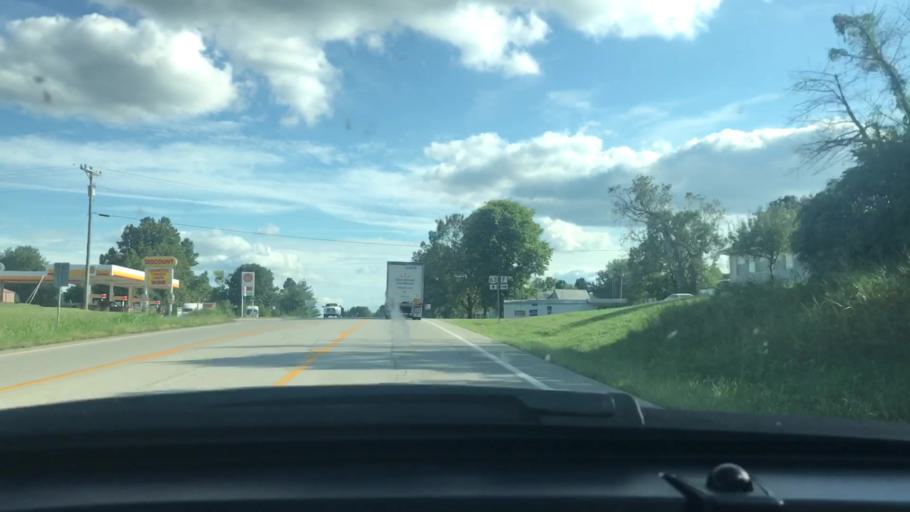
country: US
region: Missouri
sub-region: Oregon County
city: Thayer
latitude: 36.5956
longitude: -91.6440
